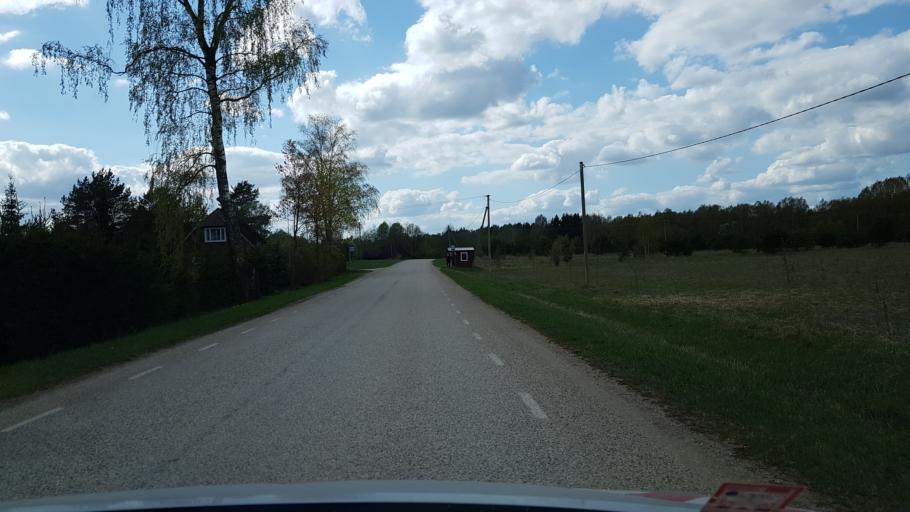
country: EE
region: Tartu
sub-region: UElenurme vald
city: Ulenurme
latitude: 58.3449
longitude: 26.8211
